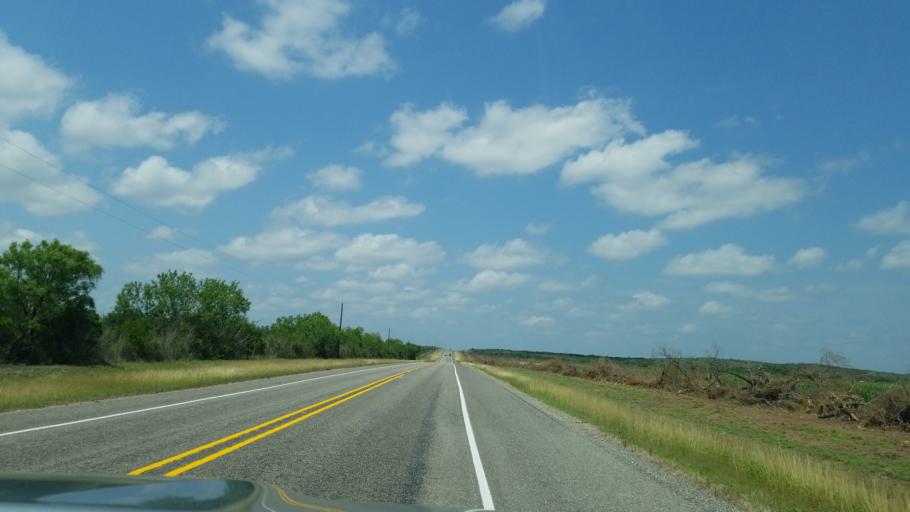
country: US
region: Texas
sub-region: Frio County
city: Pearsall
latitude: 28.9453
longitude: -99.2908
